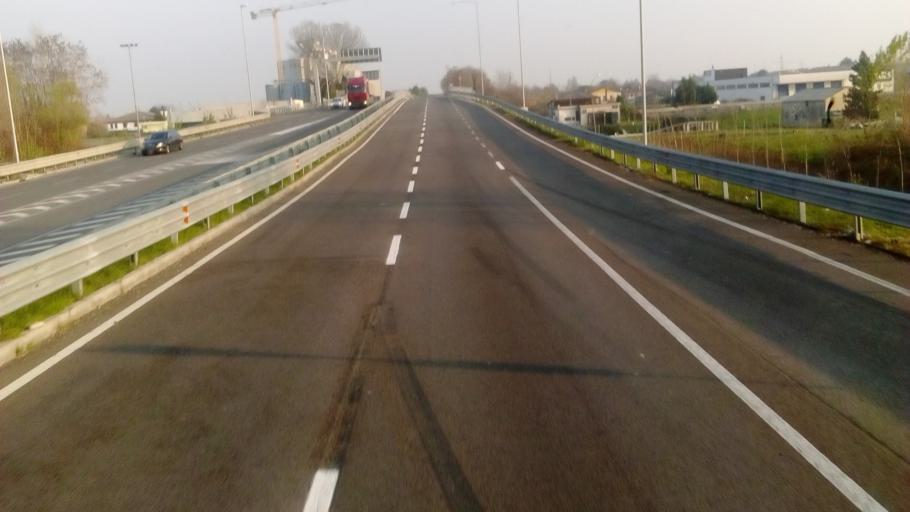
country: IT
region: Veneto
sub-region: Provincia di Padova
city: Villatora
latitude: 45.3888
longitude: 11.9541
